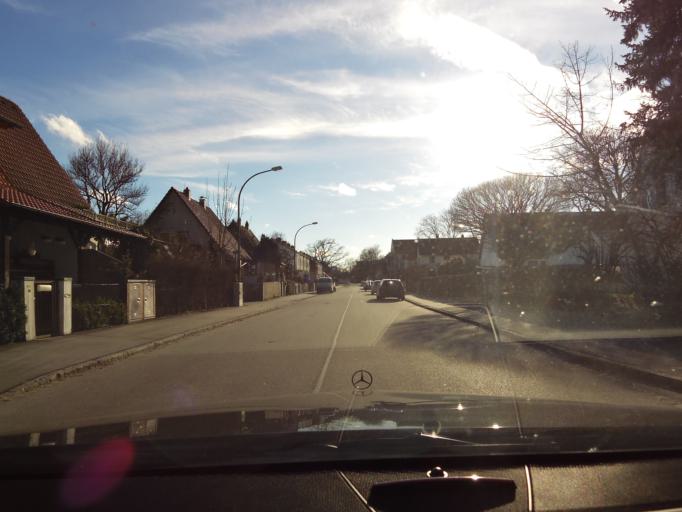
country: DE
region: Bavaria
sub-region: Lower Bavaria
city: Ergolding
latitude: 48.5524
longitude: 12.1779
